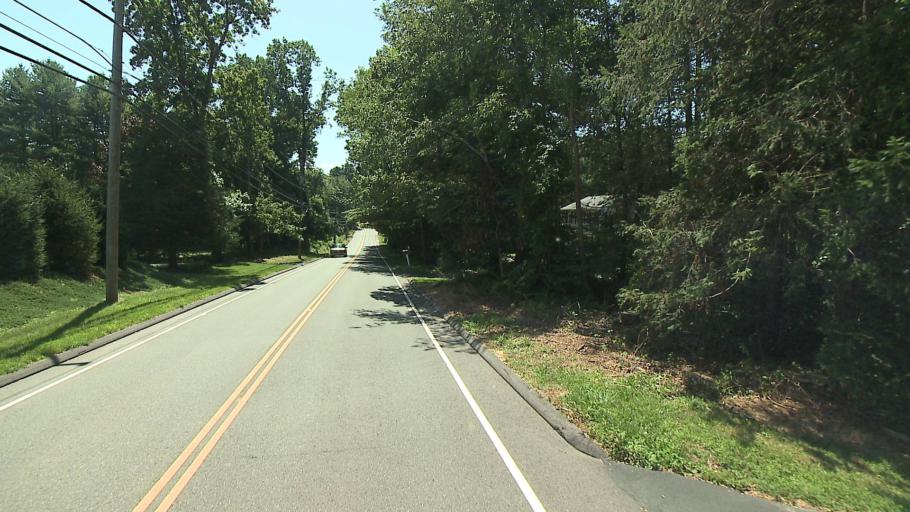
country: US
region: Connecticut
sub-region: Fairfield County
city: Trumbull
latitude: 41.3530
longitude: -73.1973
